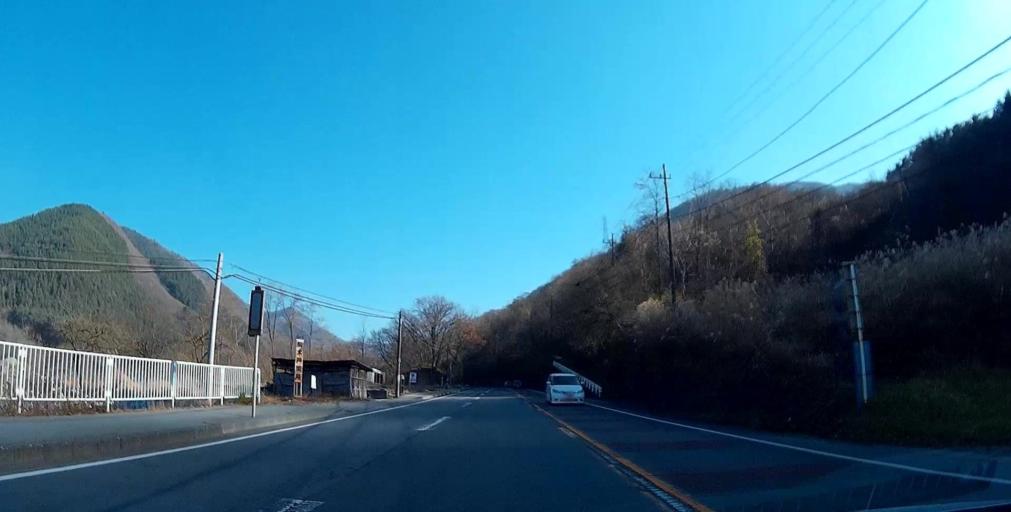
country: JP
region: Yamanashi
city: Fujikawaguchiko
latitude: 35.5907
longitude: 138.7278
